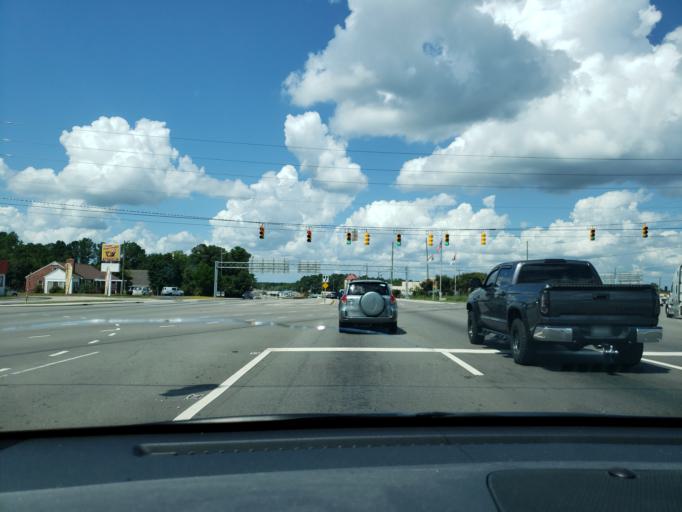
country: US
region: North Carolina
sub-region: Cumberland County
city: Spring Lake
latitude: 35.1676
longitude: -78.9728
